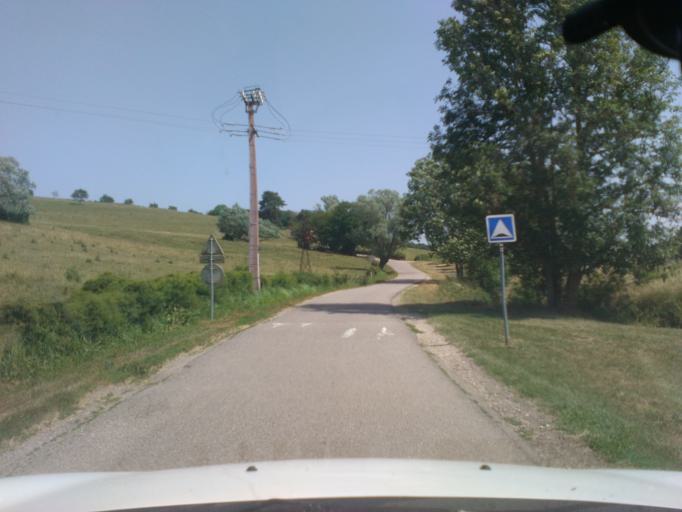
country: FR
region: Lorraine
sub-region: Departement des Vosges
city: Mirecourt
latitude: 48.3127
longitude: 6.1026
